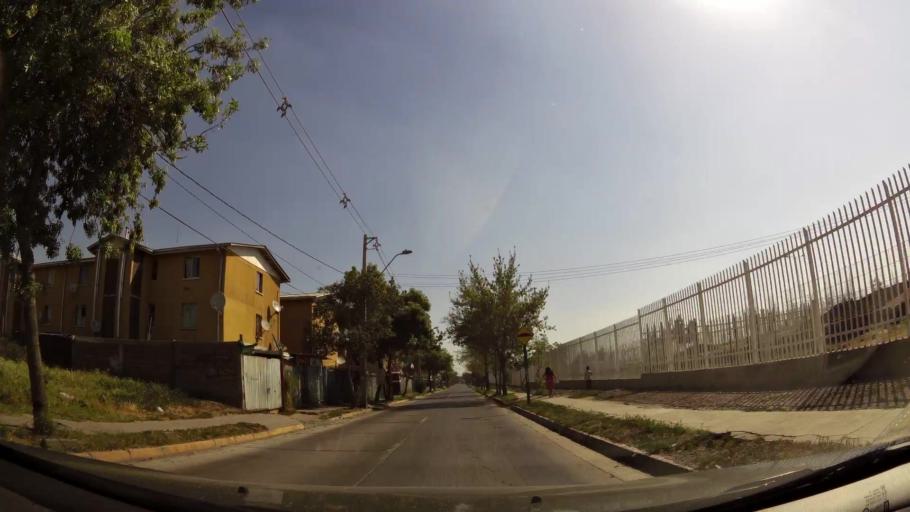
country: CL
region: Santiago Metropolitan
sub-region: Provincia de Cordillera
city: Puente Alto
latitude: -33.6257
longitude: -70.6152
